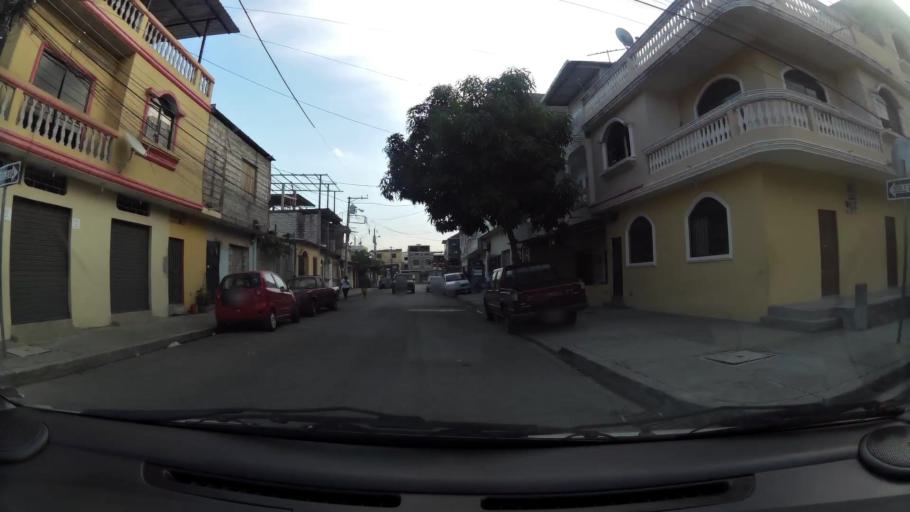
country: EC
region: Guayas
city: Eloy Alfaro
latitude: -2.1304
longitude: -79.8814
